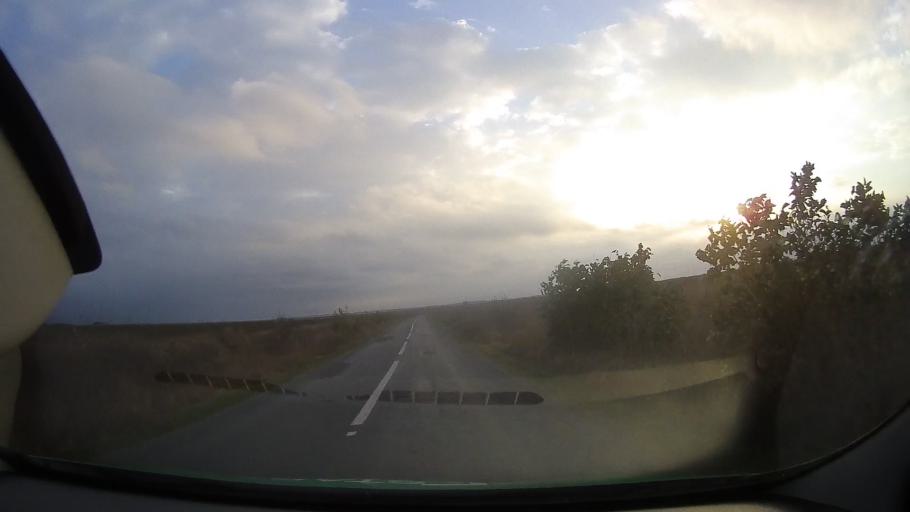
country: RO
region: Constanta
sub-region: Comuna Adamclisi
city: Adamclisi
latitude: 44.0209
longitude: 27.9067
